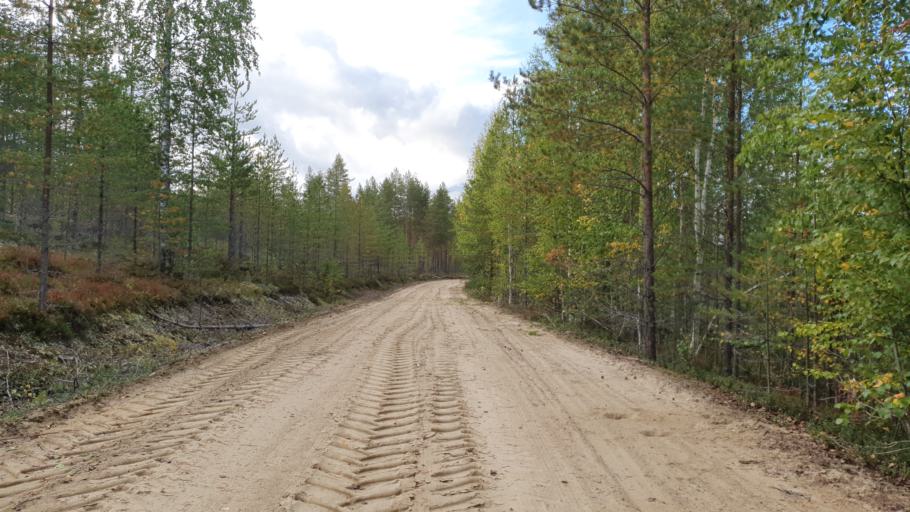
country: FI
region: Kainuu
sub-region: Kehys-Kainuu
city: Kuhmo
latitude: 64.2014
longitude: 29.1690
